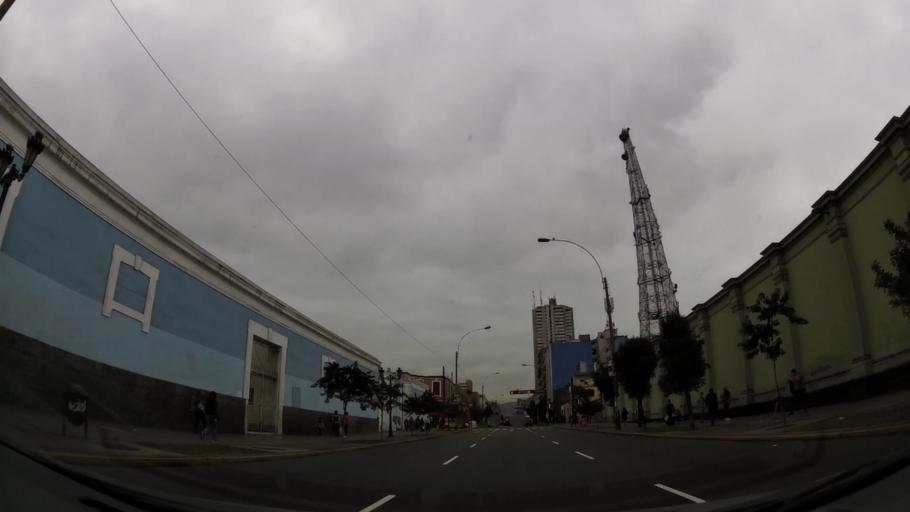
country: PE
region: Lima
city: Lima
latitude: -12.0561
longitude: -77.0411
